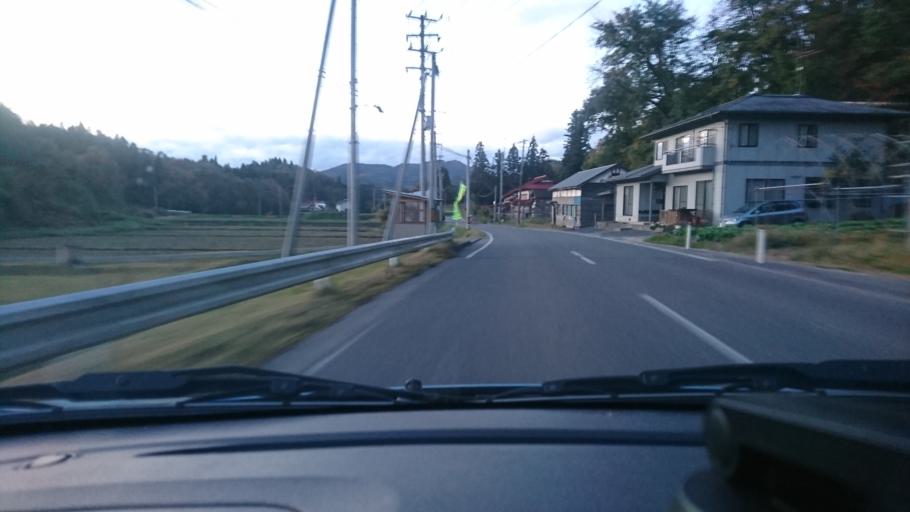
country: JP
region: Iwate
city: Ichinoseki
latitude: 38.8926
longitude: 141.3323
